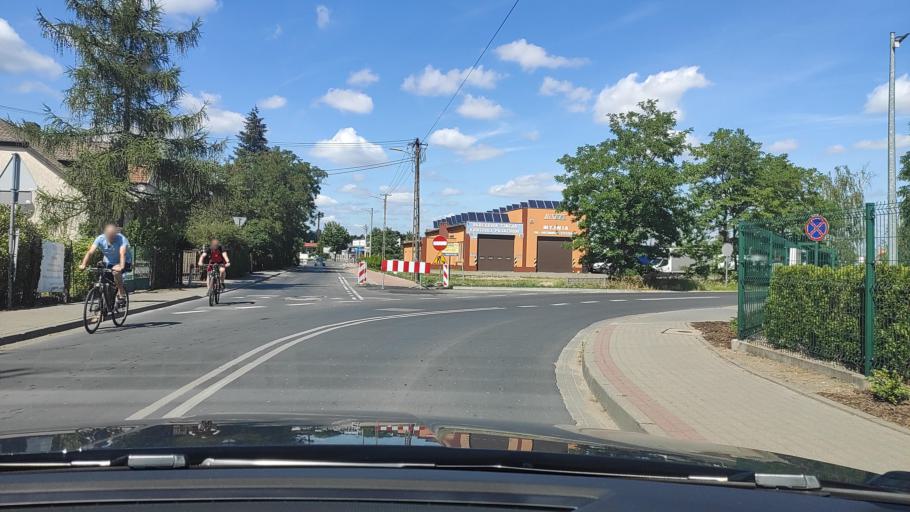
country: PL
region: Greater Poland Voivodeship
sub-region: Powiat poznanski
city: Kostrzyn
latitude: 52.4674
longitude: 17.1701
